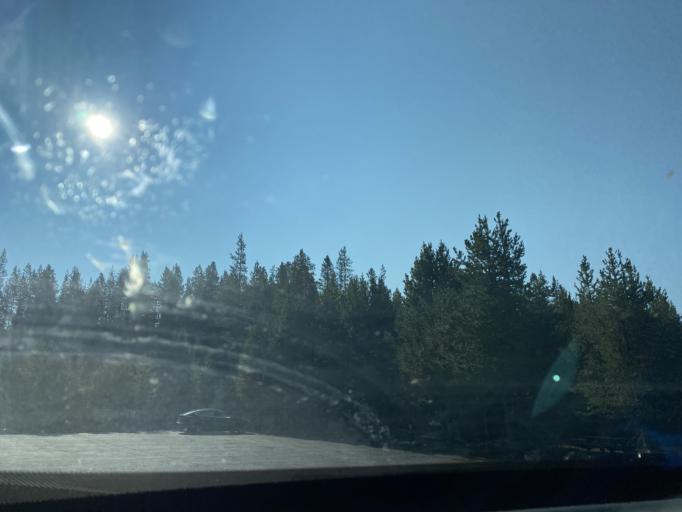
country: US
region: Oregon
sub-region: Deschutes County
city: Three Rivers
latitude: 43.7065
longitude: -121.2362
